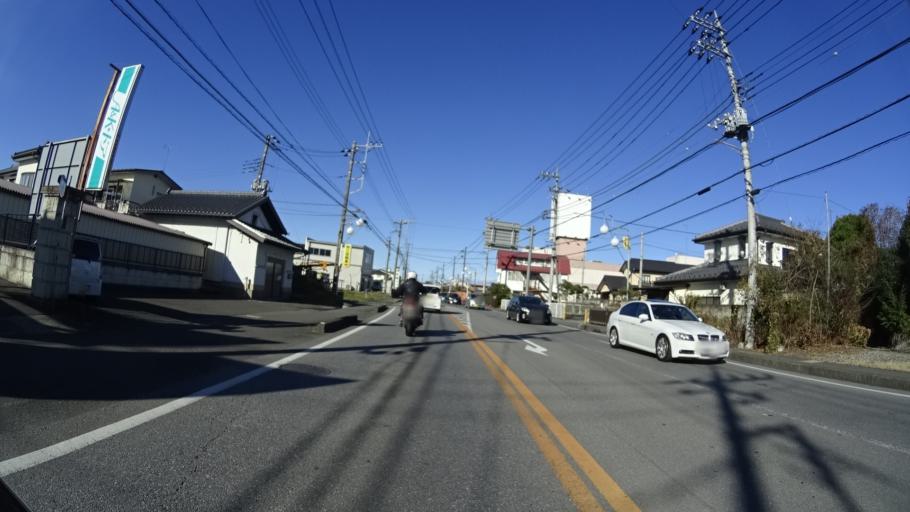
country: JP
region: Tochigi
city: Kanuma
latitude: 36.5513
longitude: 139.7471
